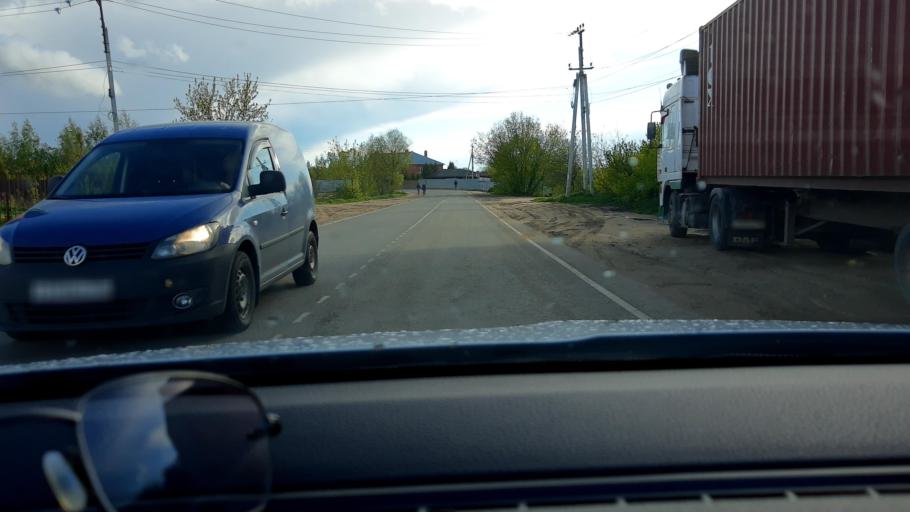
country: RU
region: Moskovskaya
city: Pavlovskaya Sloboda
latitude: 55.8168
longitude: 37.1046
